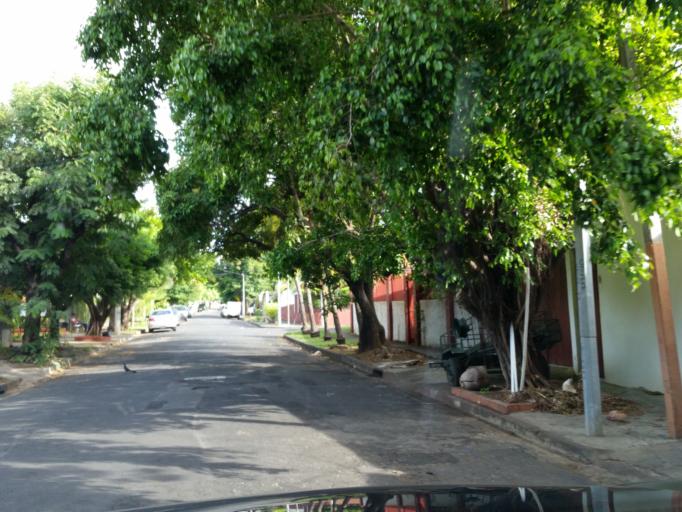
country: NI
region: Managua
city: Managua
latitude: 12.1247
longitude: -86.2558
